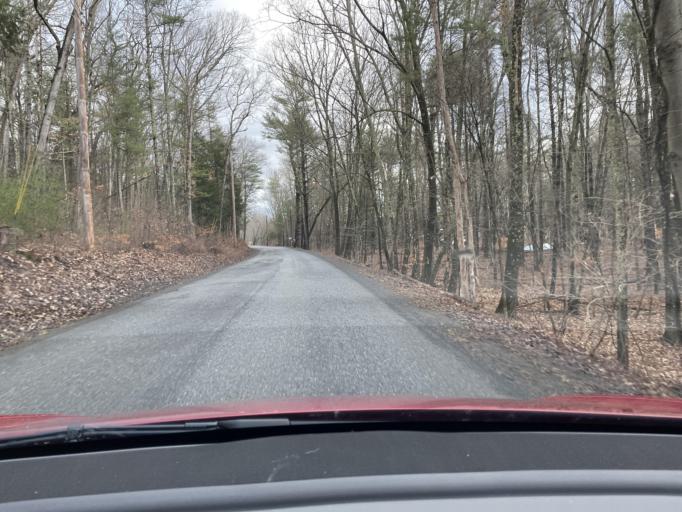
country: US
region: New York
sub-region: Ulster County
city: Zena
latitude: 42.0719
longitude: -74.0435
